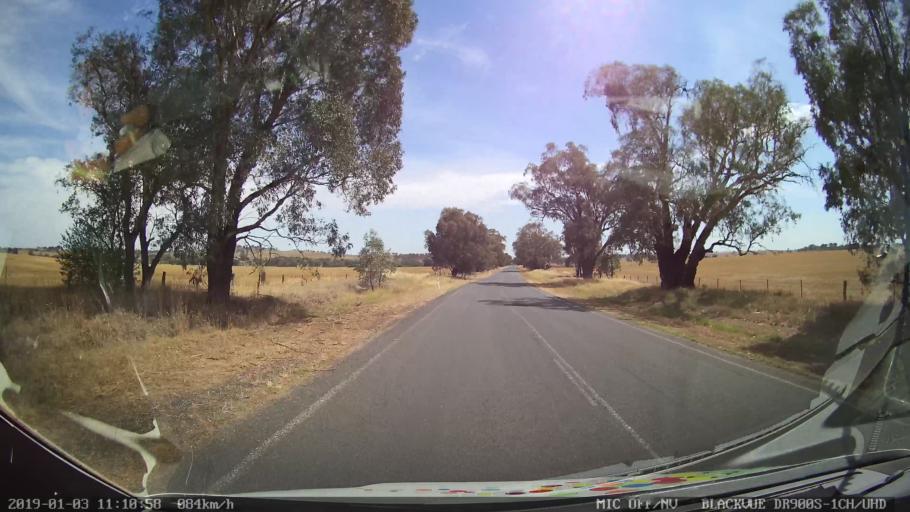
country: AU
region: New South Wales
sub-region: Young
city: Young
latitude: -34.2206
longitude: 148.2590
